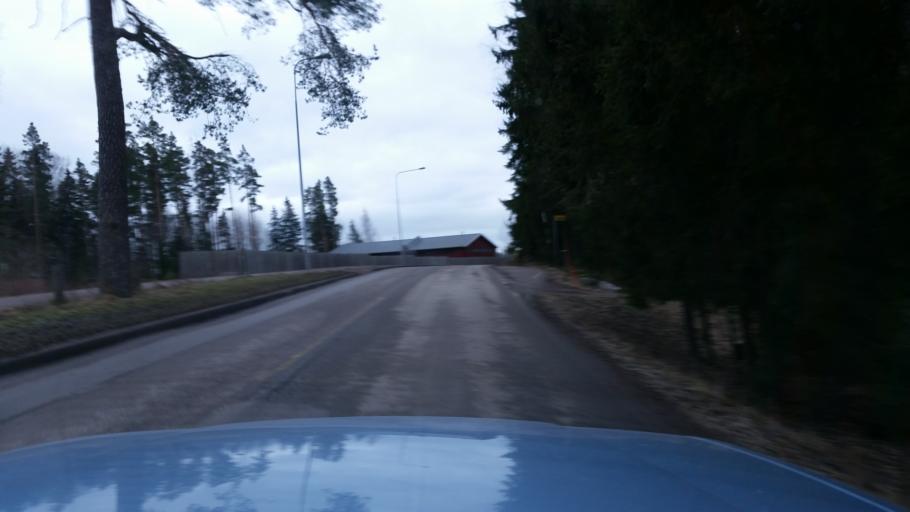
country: FI
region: Uusimaa
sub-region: Helsinki
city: Kauniainen
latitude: 60.2559
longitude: 24.7052
